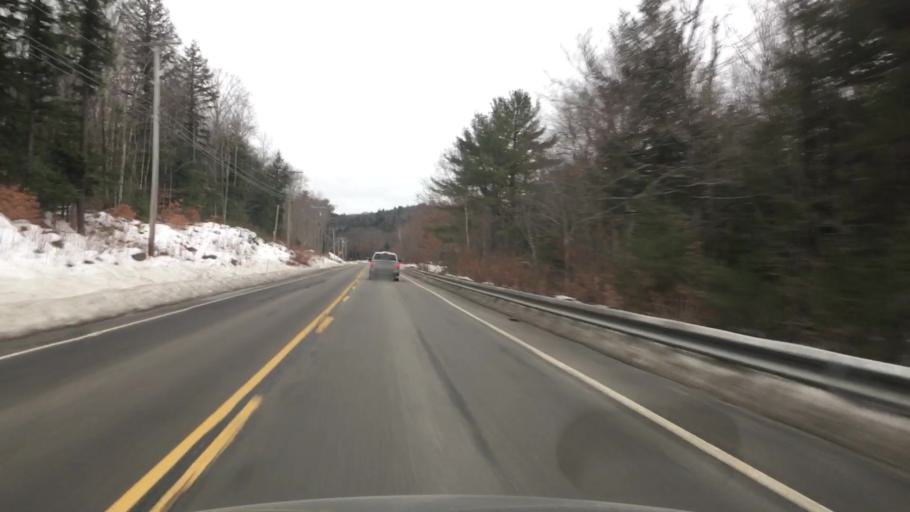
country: US
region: New Hampshire
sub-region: Merrimack County
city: Newbury
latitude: 43.3083
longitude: -72.0161
